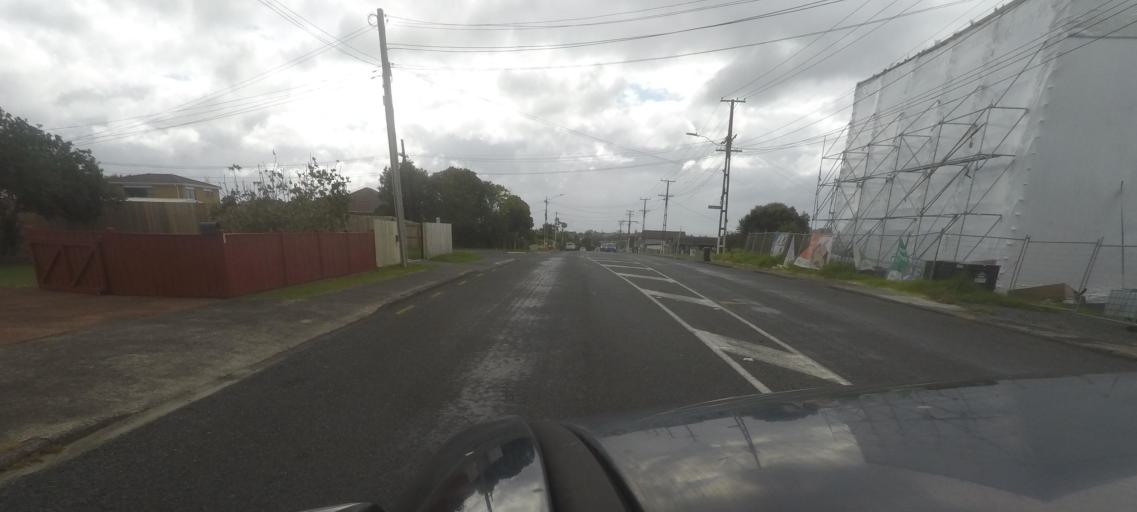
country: NZ
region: Auckland
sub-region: Auckland
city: Auckland
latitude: -36.9190
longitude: 174.7344
